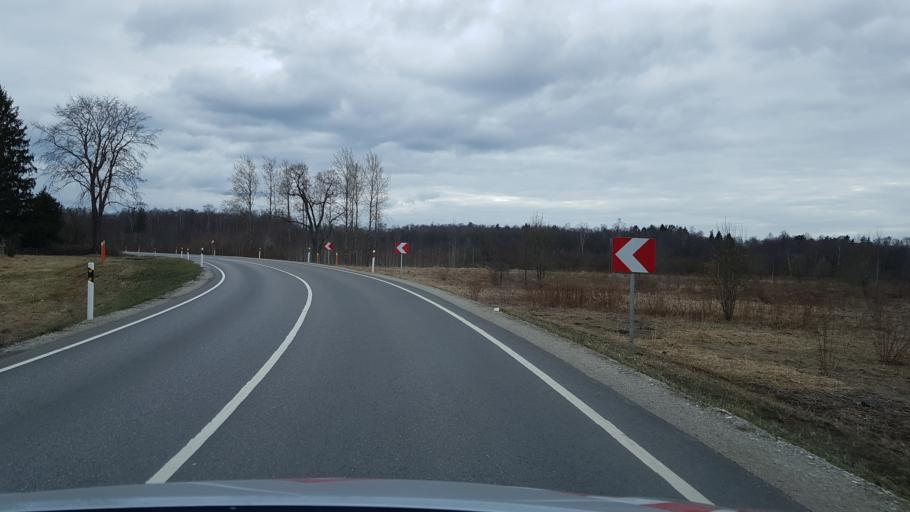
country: EE
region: Ida-Virumaa
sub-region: Narva-Joesuu linn
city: Narva-Joesuu
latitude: 59.4116
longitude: 28.0697
